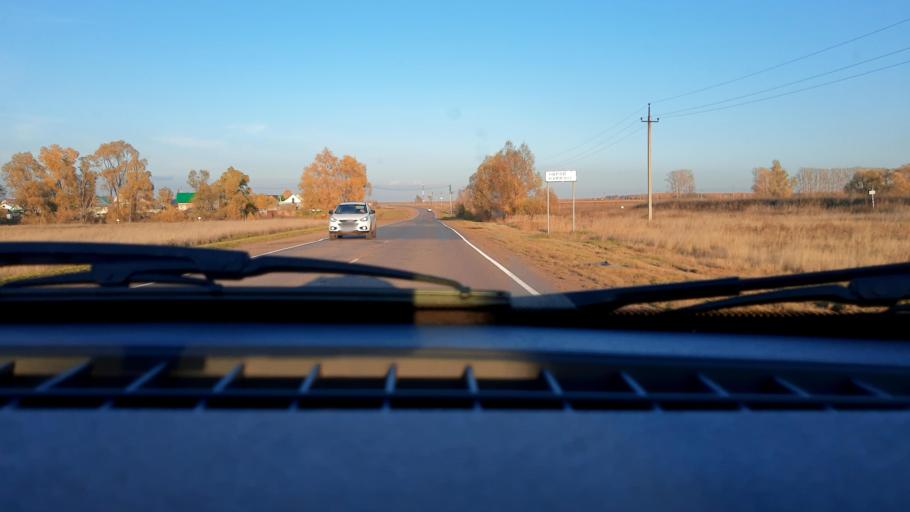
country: RU
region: Bashkortostan
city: Asanovo
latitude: 54.8054
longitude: 55.5581
